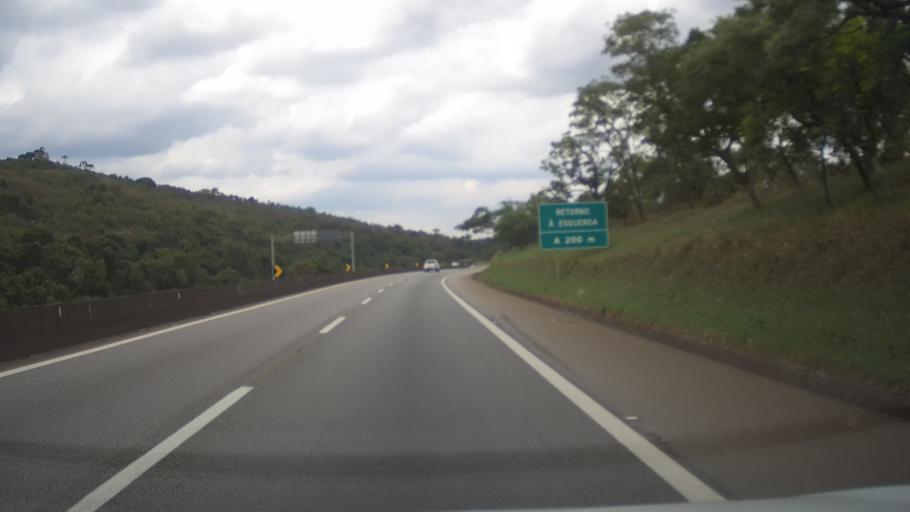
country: BR
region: Minas Gerais
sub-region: Tres Coracoes
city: Tres Coracoes
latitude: -21.5297
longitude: -45.2302
